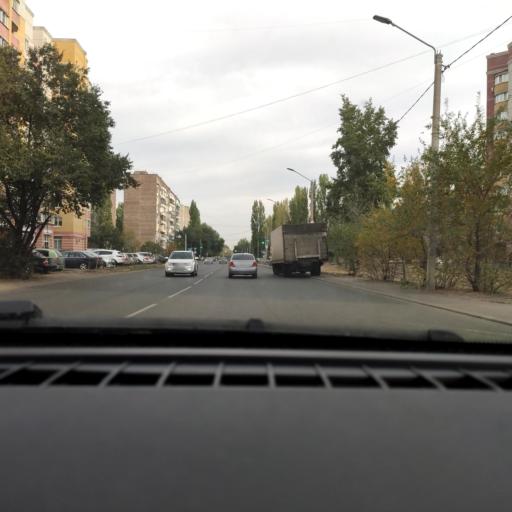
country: RU
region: Voronezj
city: Maslovka
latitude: 51.5938
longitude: 39.2438
